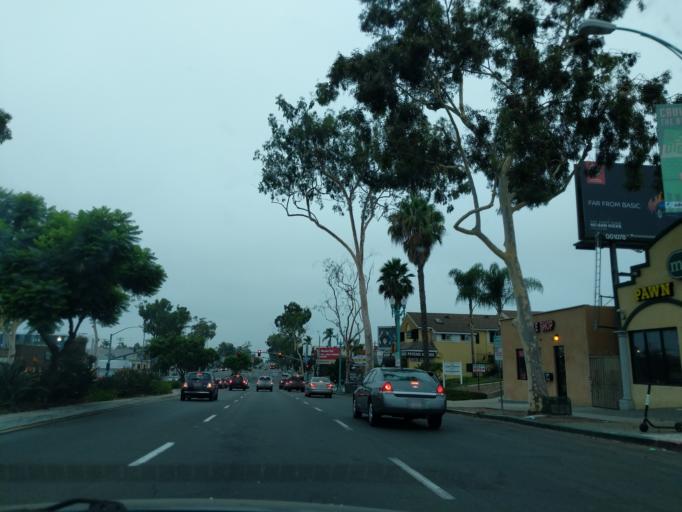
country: US
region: California
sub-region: San Diego County
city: San Diego
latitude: 32.7554
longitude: -117.1263
